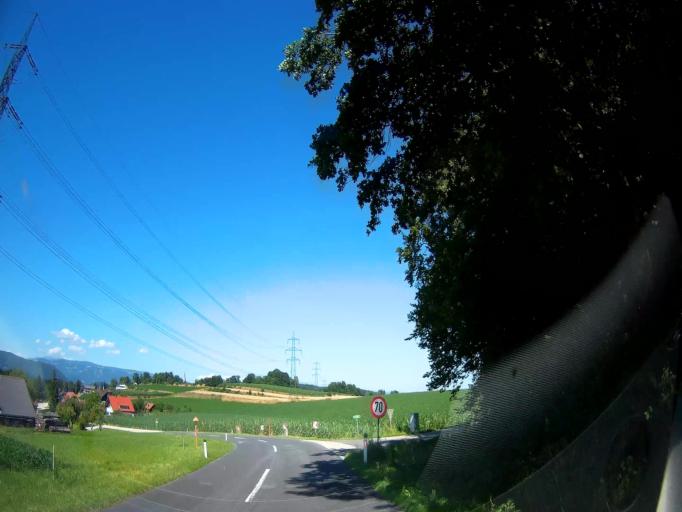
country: AT
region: Carinthia
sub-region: Politischer Bezirk Volkermarkt
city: Gallizien
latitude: 46.6025
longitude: 14.5335
